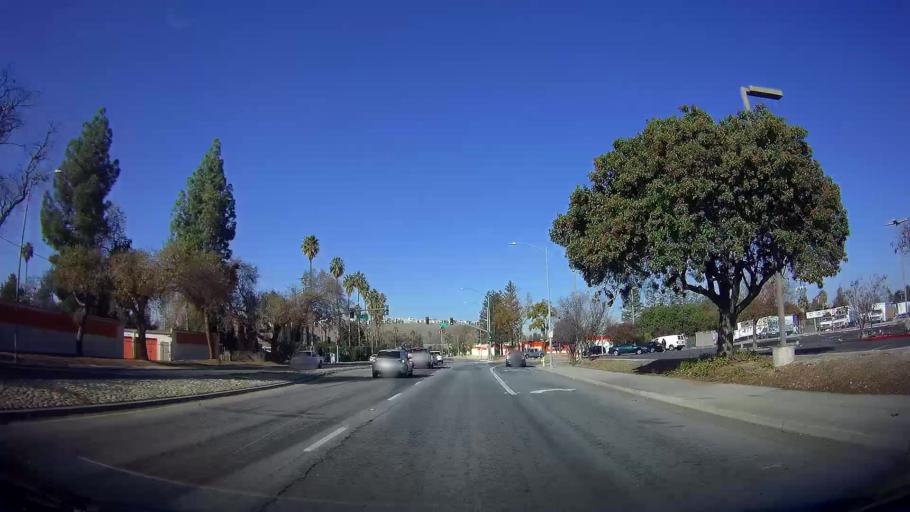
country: US
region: California
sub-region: Santa Clara County
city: Seven Trees
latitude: 37.2782
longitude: -121.8429
